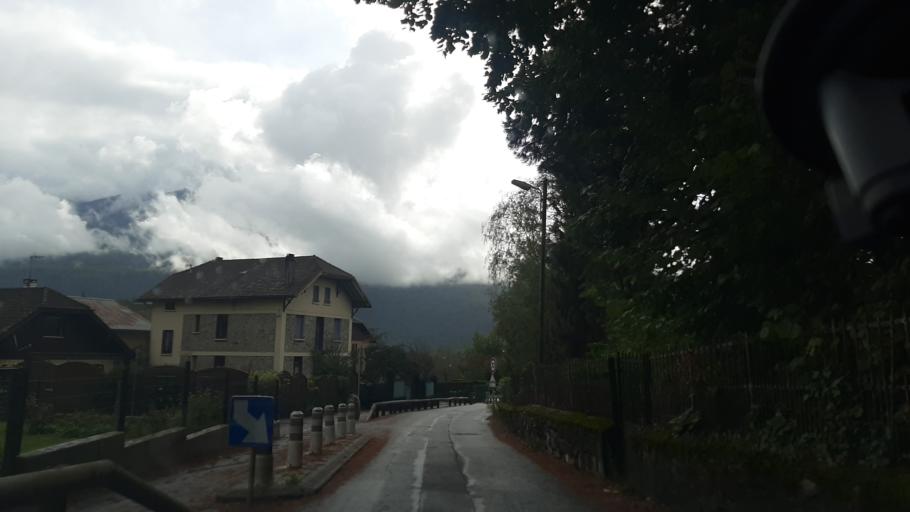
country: FR
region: Rhone-Alpes
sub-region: Departement de la Savoie
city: Gresy-sur-Isere
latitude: 45.5991
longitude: 6.2571
